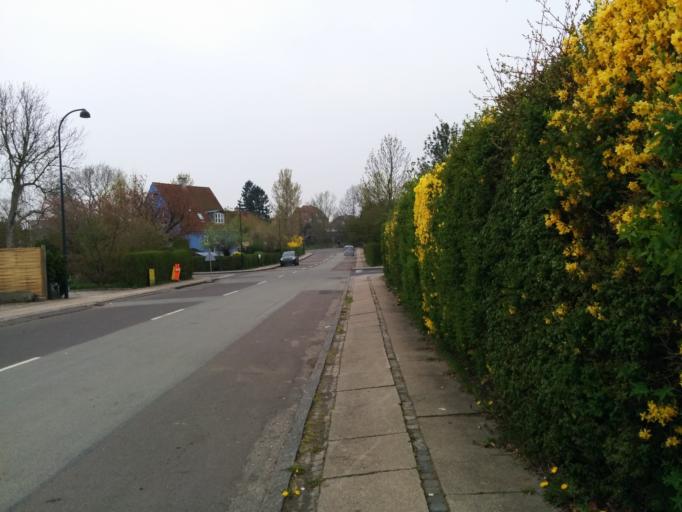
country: DK
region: Capital Region
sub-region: Frederiksberg Kommune
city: Frederiksberg
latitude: 55.7281
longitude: 12.5287
